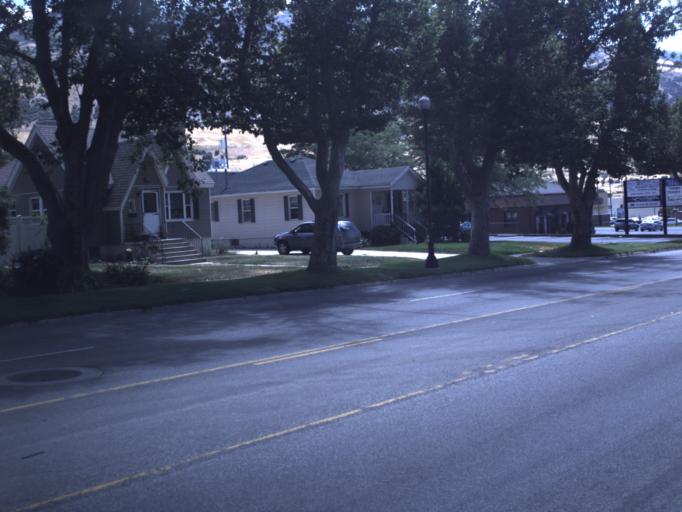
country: US
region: Utah
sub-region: Box Elder County
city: Brigham City
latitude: 41.4972
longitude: -112.0161
